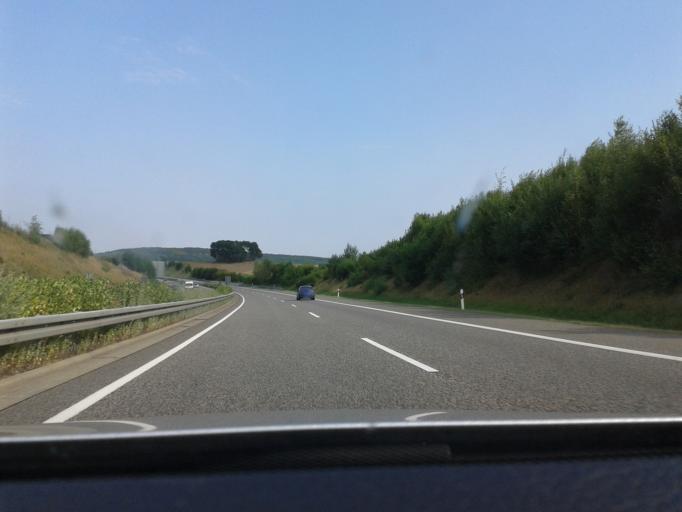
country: DE
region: Thuringia
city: Schachtebich
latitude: 51.3947
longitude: 10.0452
